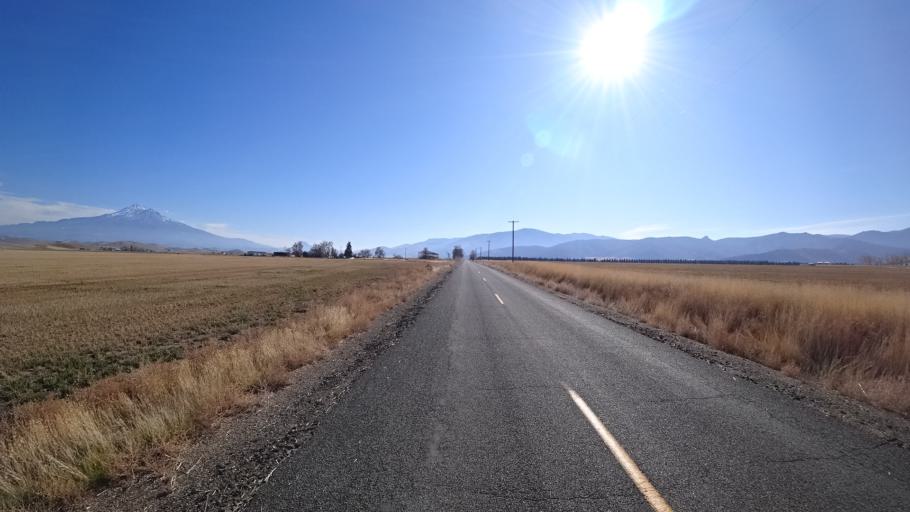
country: US
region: California
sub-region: Siskiyou County
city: Montague
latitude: 41.5625
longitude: -122.5478
